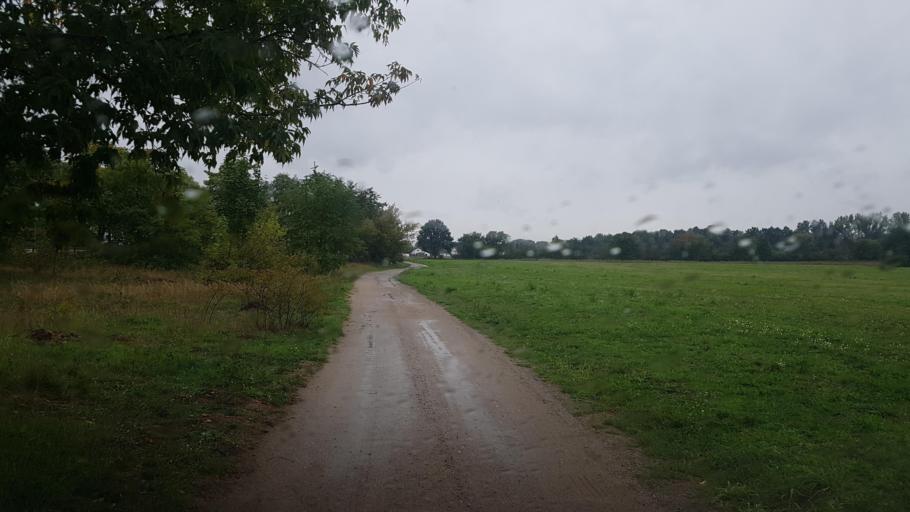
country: DE
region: Brandenburg
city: Elsterwerda
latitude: 51.4626
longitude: 13.5003
